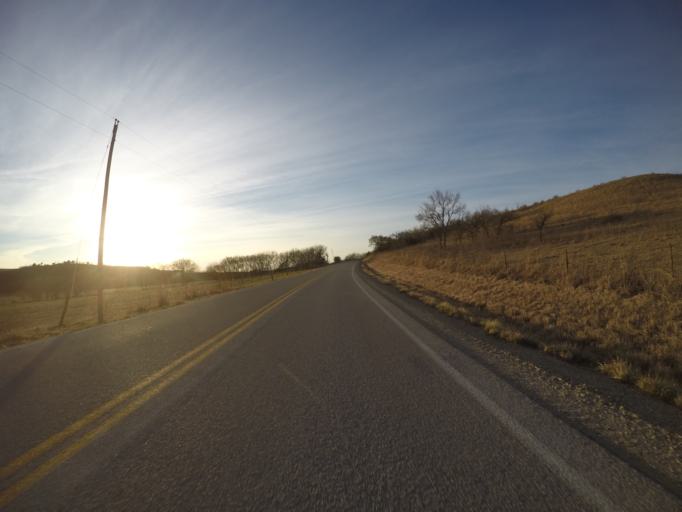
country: US
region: Kansas
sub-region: Riley County
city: Manhattan
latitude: 39.3014
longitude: -96.7078
